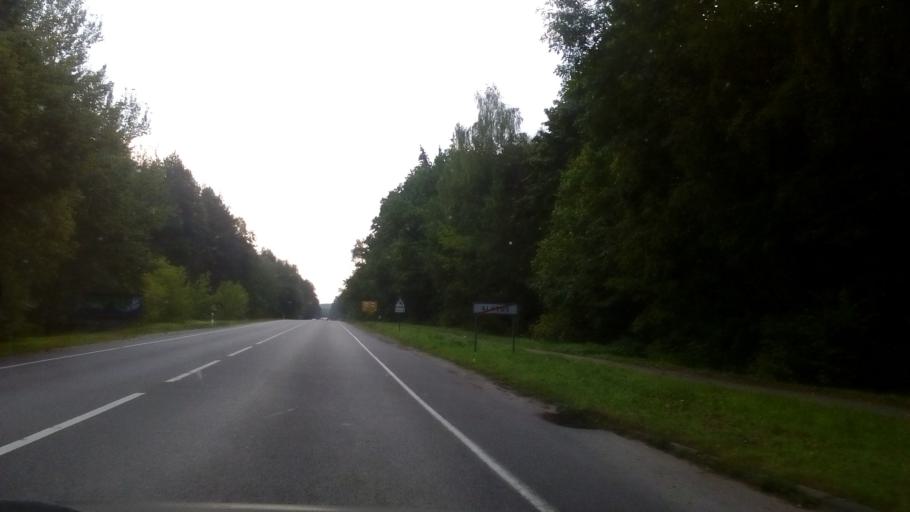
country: LT
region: Alytaus apskritis
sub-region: Alytus
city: Alytus
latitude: 54.3787
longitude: 24.0653
